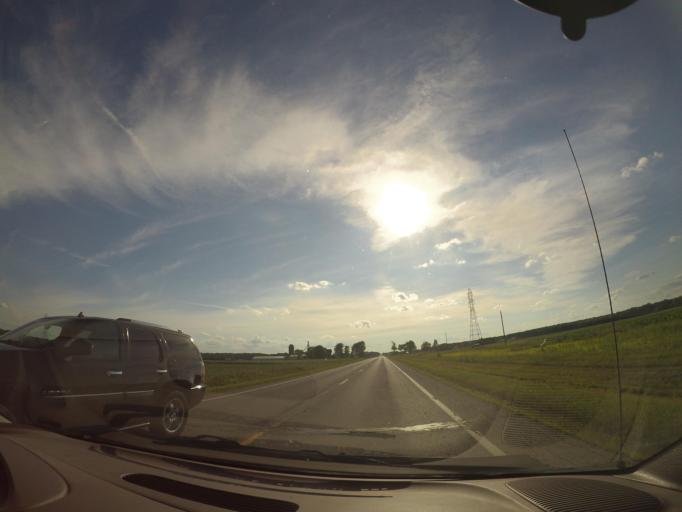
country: US
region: Ohio
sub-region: Fulton County
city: Archbold
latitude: 41.4422
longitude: -84.3331
